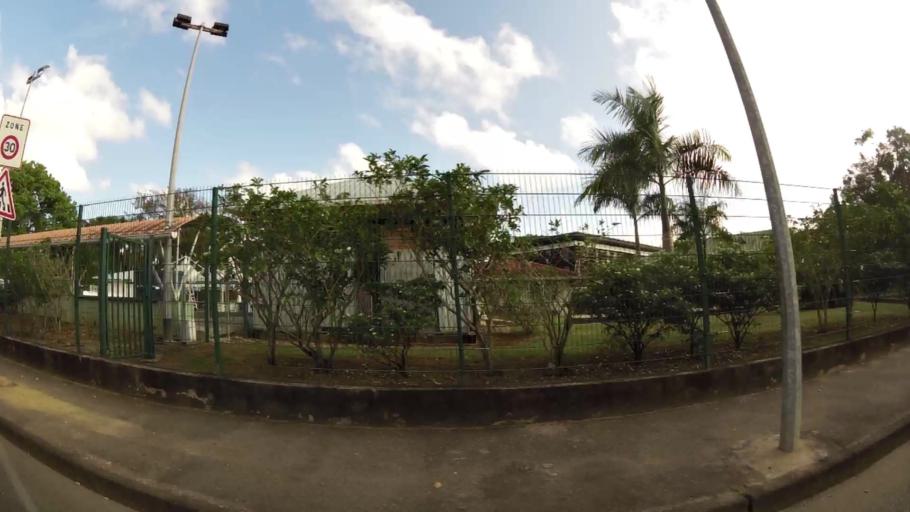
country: GF
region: Guyane
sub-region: Guyane
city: Cayenne
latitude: 4.9391
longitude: -52.3188
